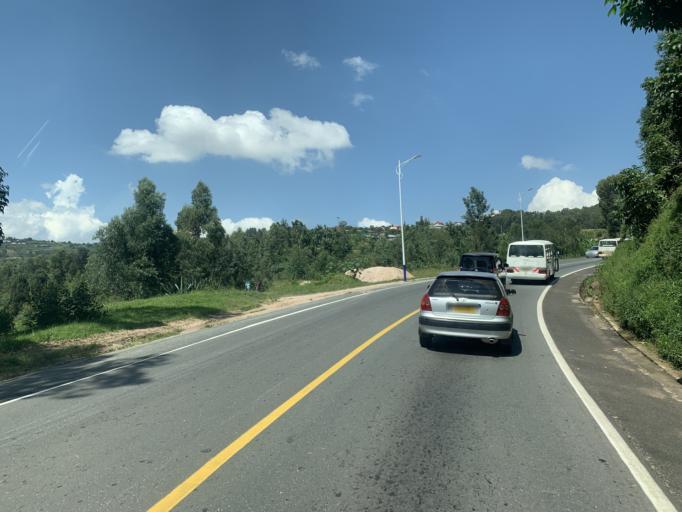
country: RW
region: Southern Province
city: Gitarama
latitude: -2.0571
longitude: 29.8038
